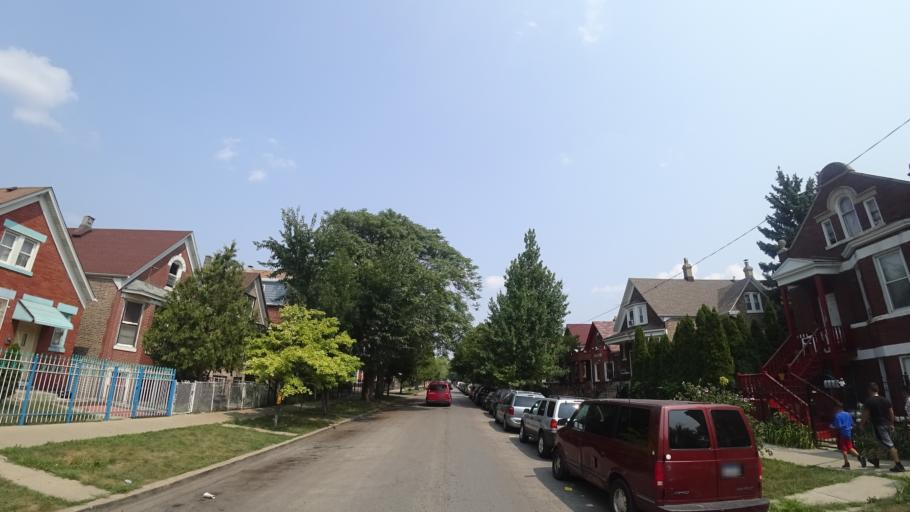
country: US
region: Illinois
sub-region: Cook County
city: Cicero
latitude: 41.8425
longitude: -87.7233
